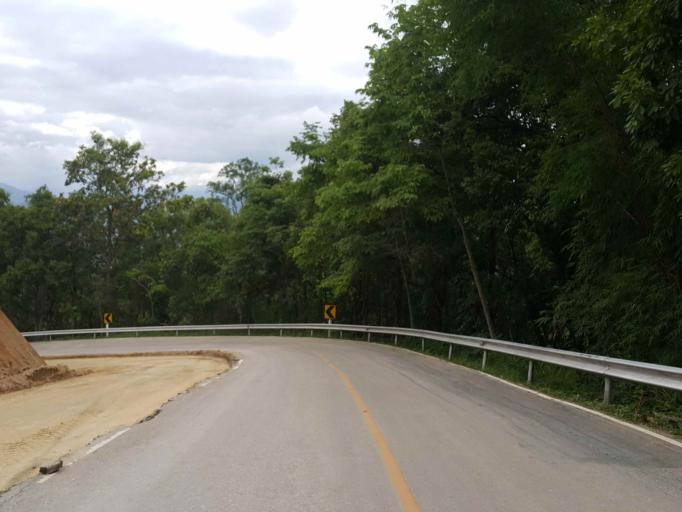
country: TH
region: Chiang Mai
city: Mae Chaem
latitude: 18.5093
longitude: 98.4352
